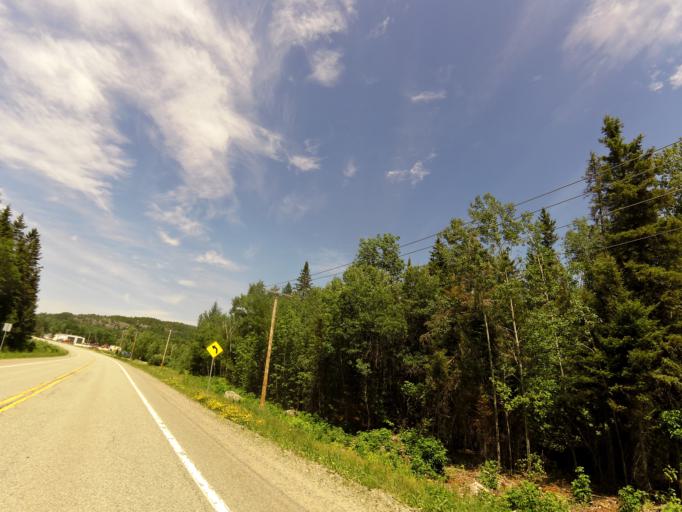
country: CA
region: Quebec
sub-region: Abitibi-Temiscamingue
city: Ville-Marie
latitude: 47.2928
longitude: -79.4206
